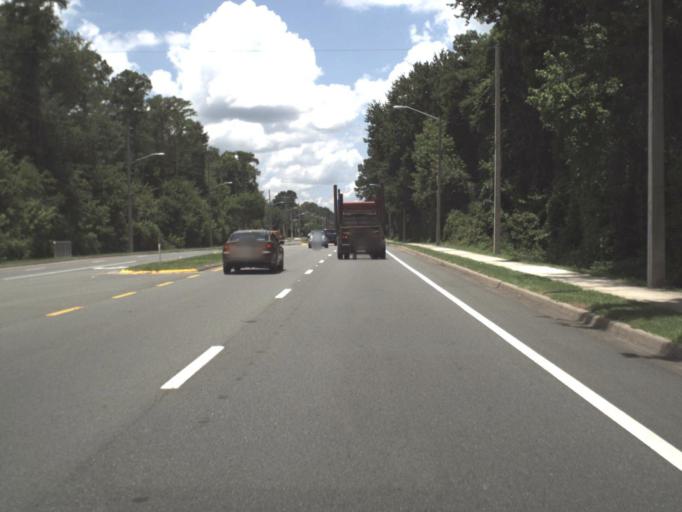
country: US
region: Florida
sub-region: Alachua County
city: Gainesville
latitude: 29.6884
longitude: -82.3021
